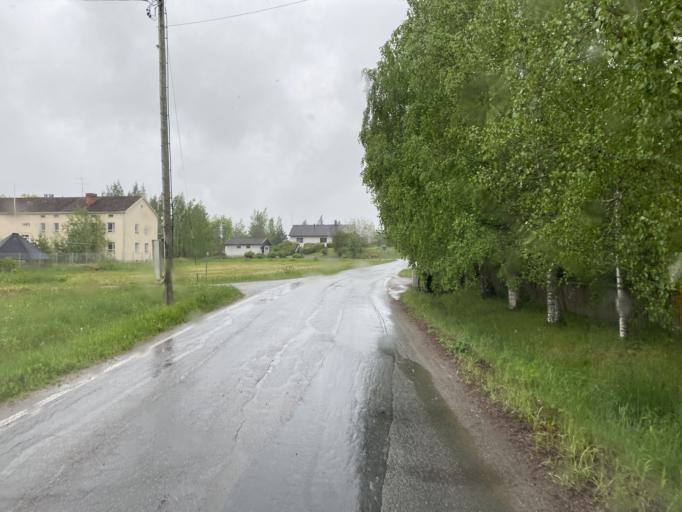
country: FI
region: Haeme
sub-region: Forssa
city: Humppila
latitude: 61.0967
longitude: 23.3166
